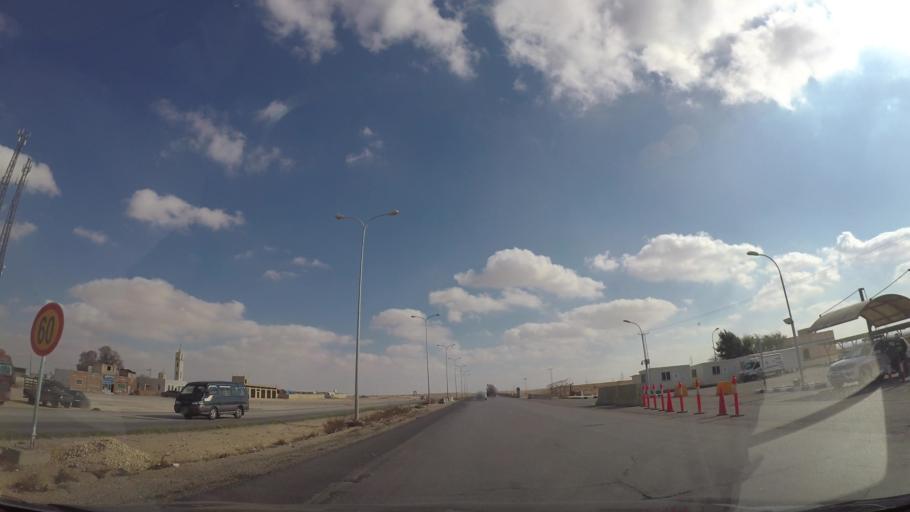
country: JO
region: Amman
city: Al Jizah
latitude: 31.4927
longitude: 36.0590
